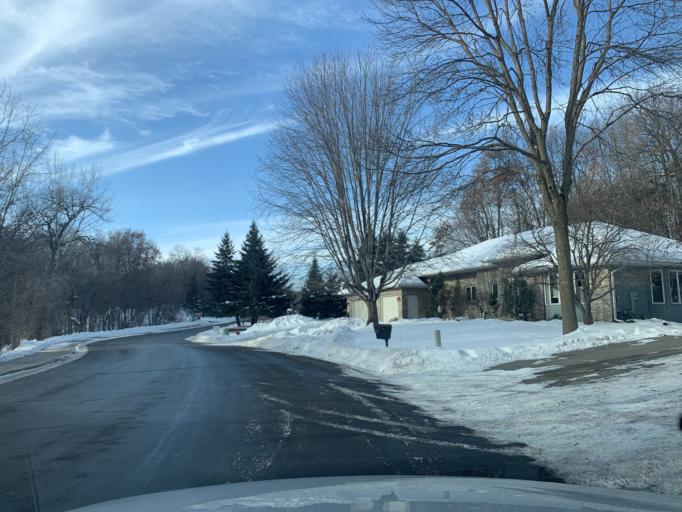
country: US
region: Minnesota
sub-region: Wright County
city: Saint Michael
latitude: 45.2043
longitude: -93.6577
